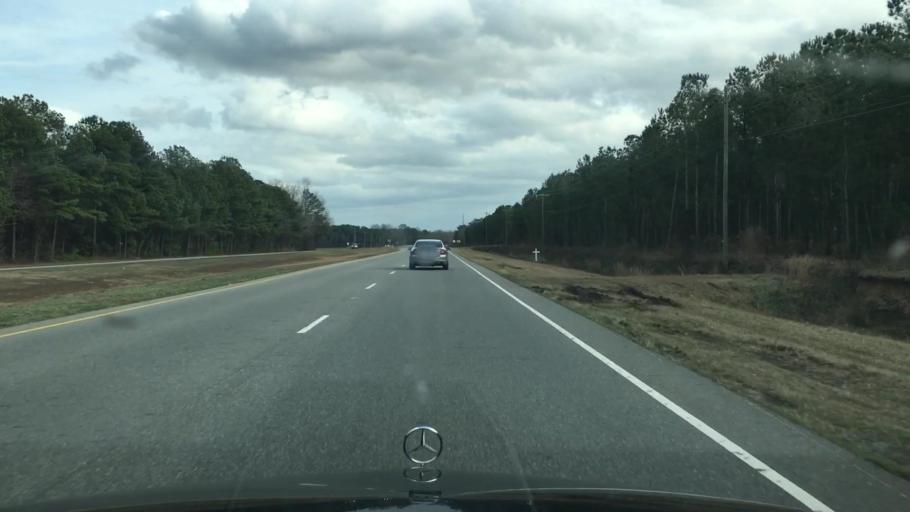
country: US
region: North Carolina
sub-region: Duplin County
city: Kenansville
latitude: 34.9500
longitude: -77.8894
